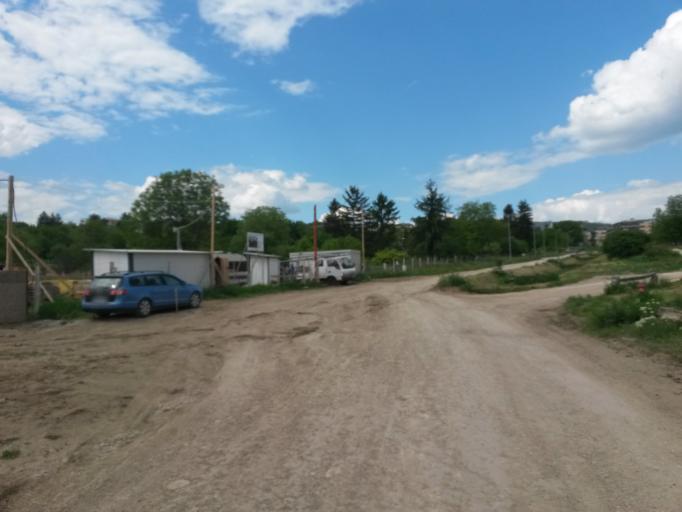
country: HU
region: Budapest
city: Budapest XII. keruelet
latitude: 47.4641
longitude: 18.9936
